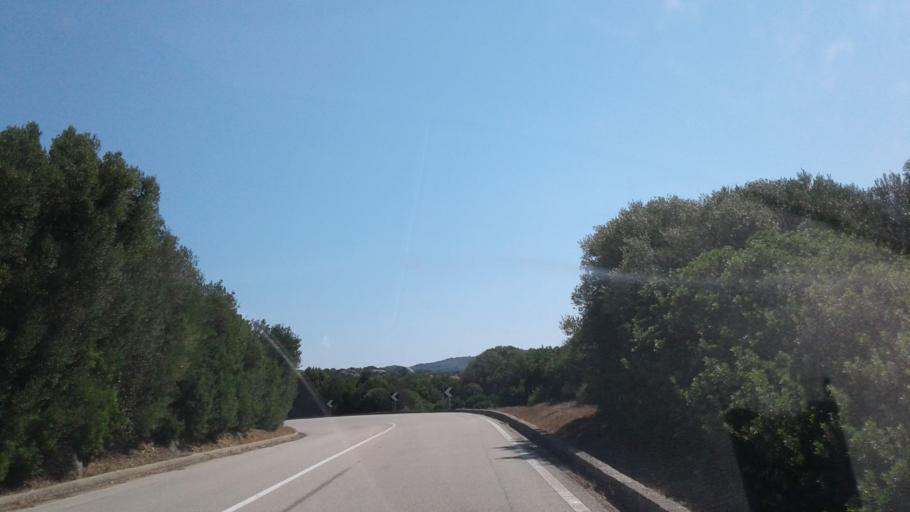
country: IT
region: Sardinia
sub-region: Provincia di Olbia-Tempio
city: Palau
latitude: 41.1270
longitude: 9.2839
